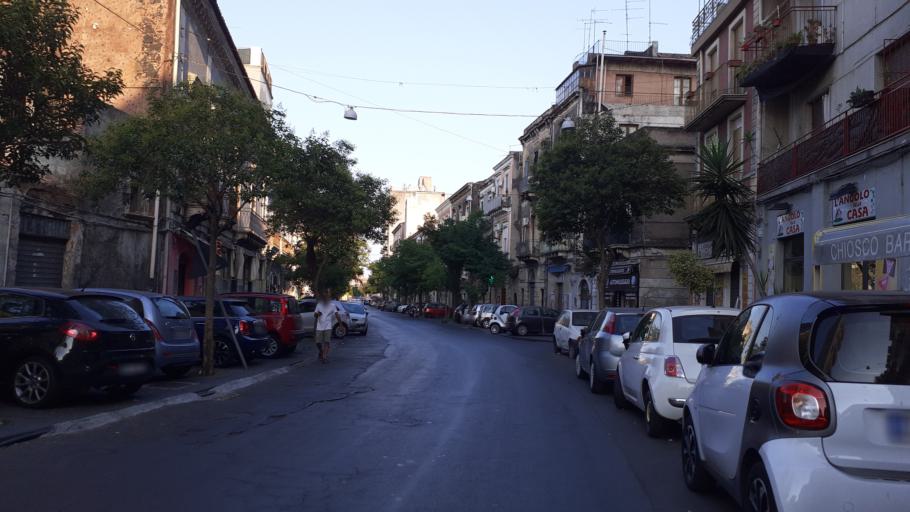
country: IT
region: Sicily
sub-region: Catania
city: Catania
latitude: 37.4992
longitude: 15.0775
